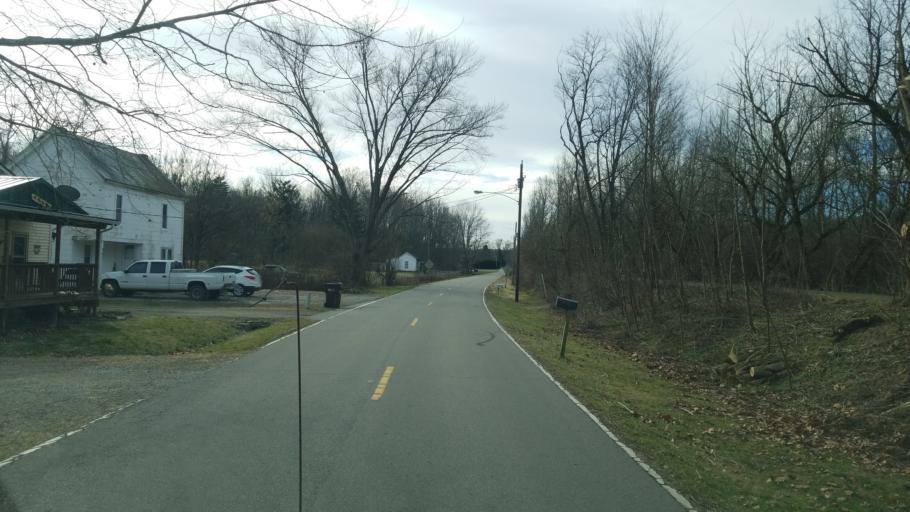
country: US
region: Ohio
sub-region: Warren County
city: Waynesville
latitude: 39.4490
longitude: -84.0971
